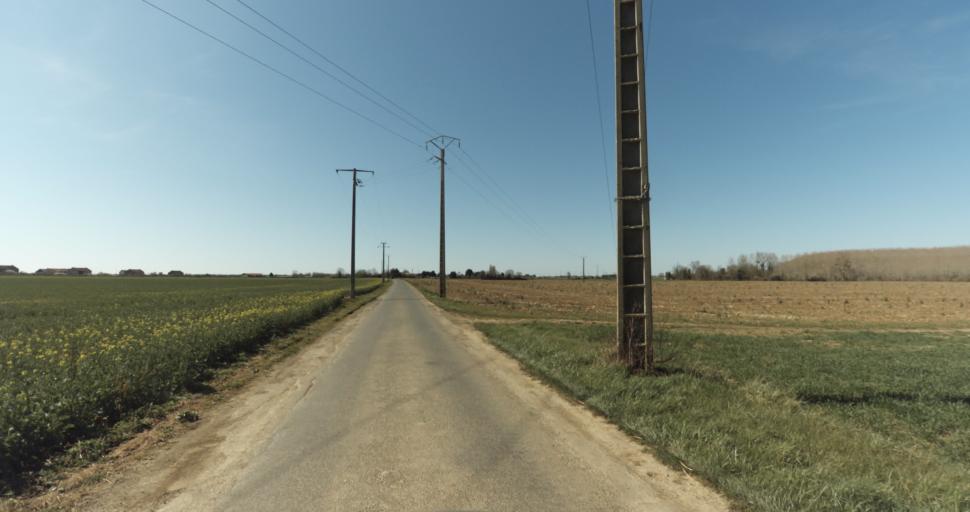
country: FR
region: Lower Normandy
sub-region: Departement du Calvados
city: Saint-Pierre-sur-Dives
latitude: 49.0509
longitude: -0.0405
